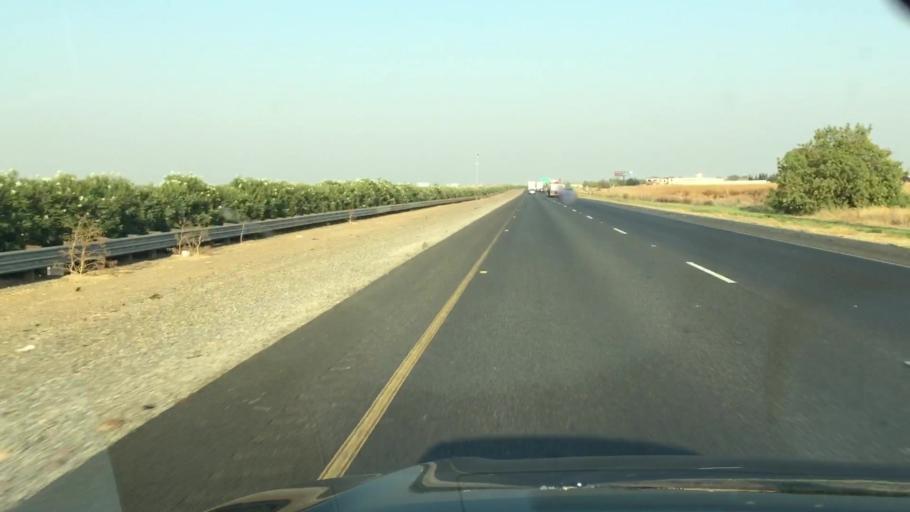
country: US
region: California
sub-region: Yolo County
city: West Sacramento
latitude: 38.6711
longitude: -121.5588
